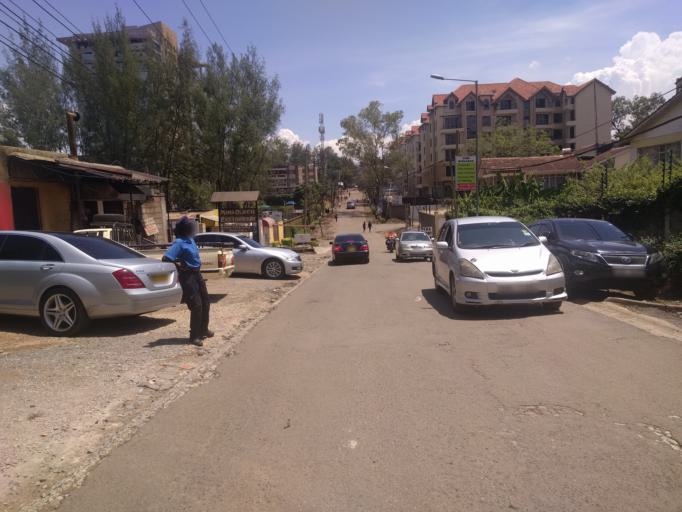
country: KE
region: Nairobi Area
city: Nairobi
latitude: -1.2941
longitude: 36.7910
